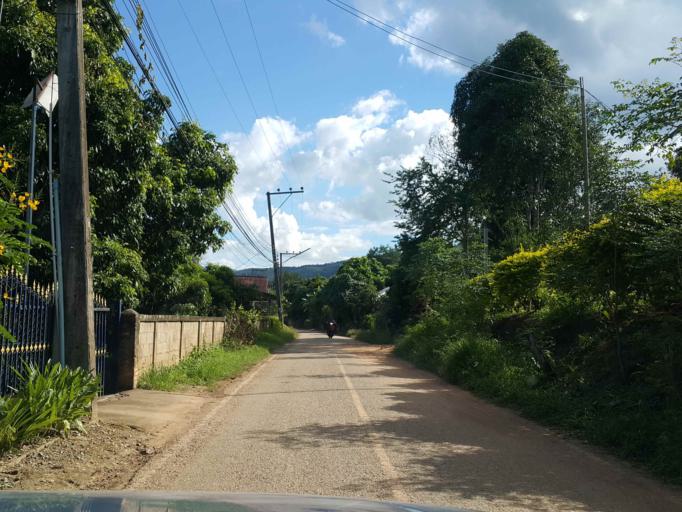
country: TH
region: Chiang Mai
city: Mae Taeng
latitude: 18.9679
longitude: 98.8978
